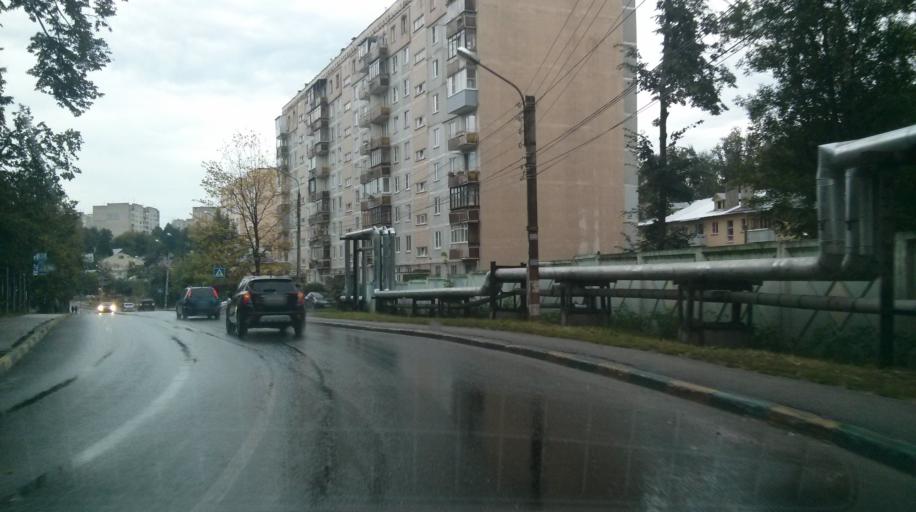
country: RU
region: Nizjnij Novgorod
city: Nizhniy Novgorod
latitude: 56.2558
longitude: 43.9742
